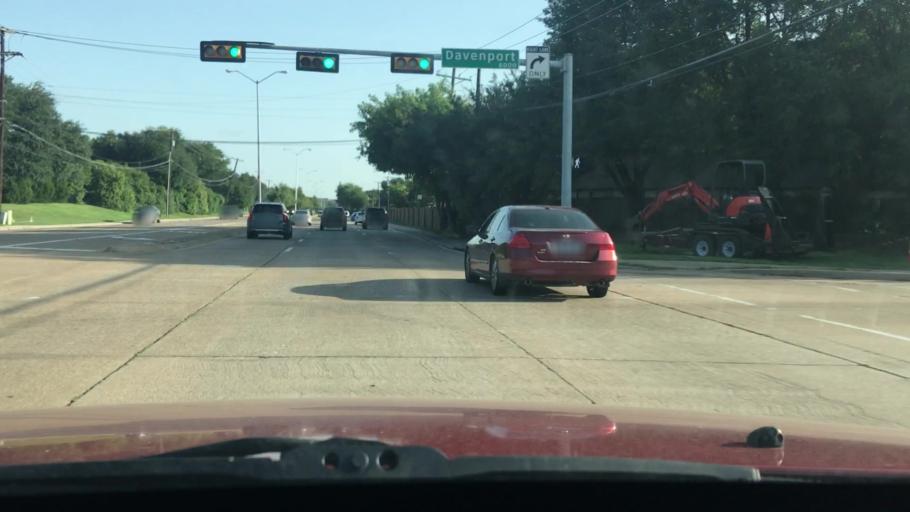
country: US
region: Texas
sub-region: Dallas County
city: Addison
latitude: 32.9761
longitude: -96.8044
